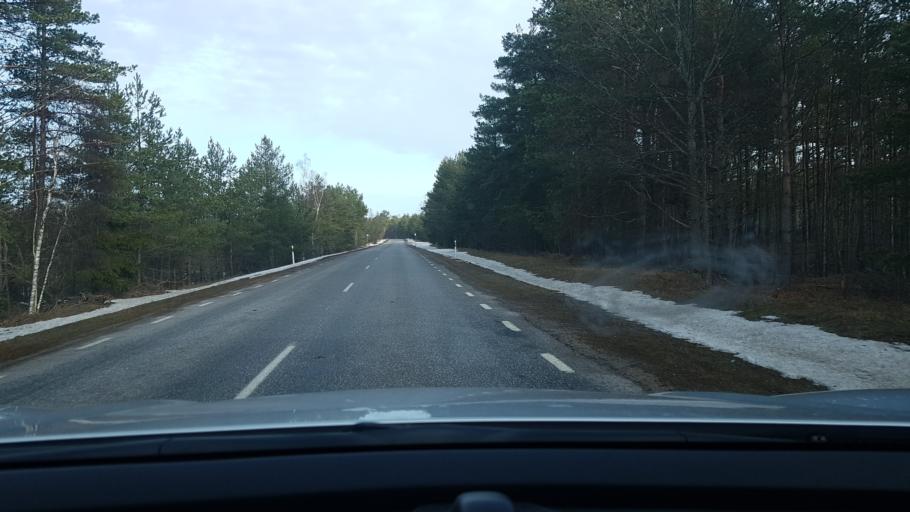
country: EE
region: Saare
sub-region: Kuressaare linn
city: Kuressaare
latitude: 58.4431
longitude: 22.7060
